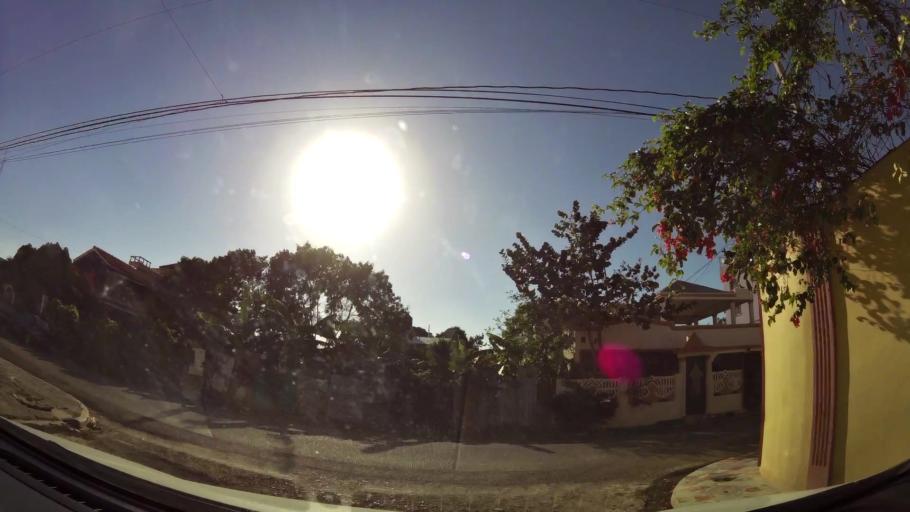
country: DO
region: Santo Domingo
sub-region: Santo Domingo
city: Santo Domingo Este
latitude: 18.4868
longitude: -69.8058
